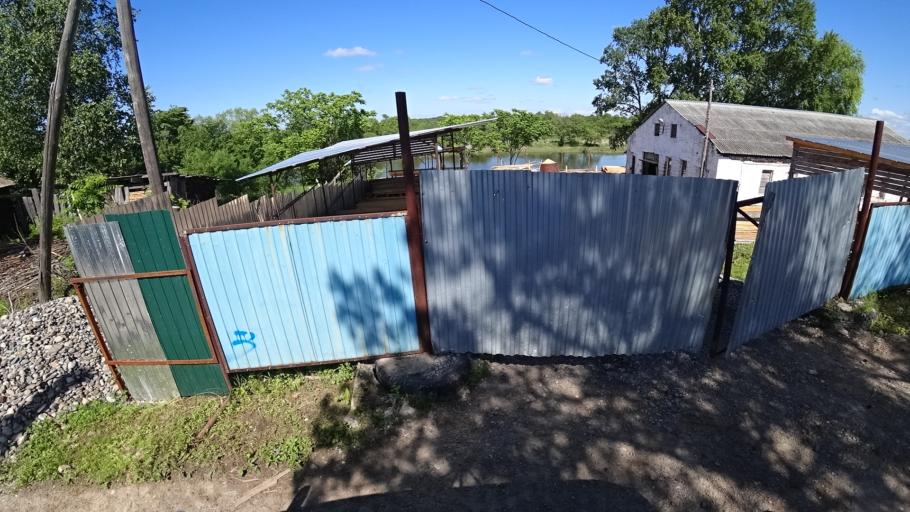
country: RU
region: Khabarovsk Krai
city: Khor
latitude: 47.8855
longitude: 135.0375
